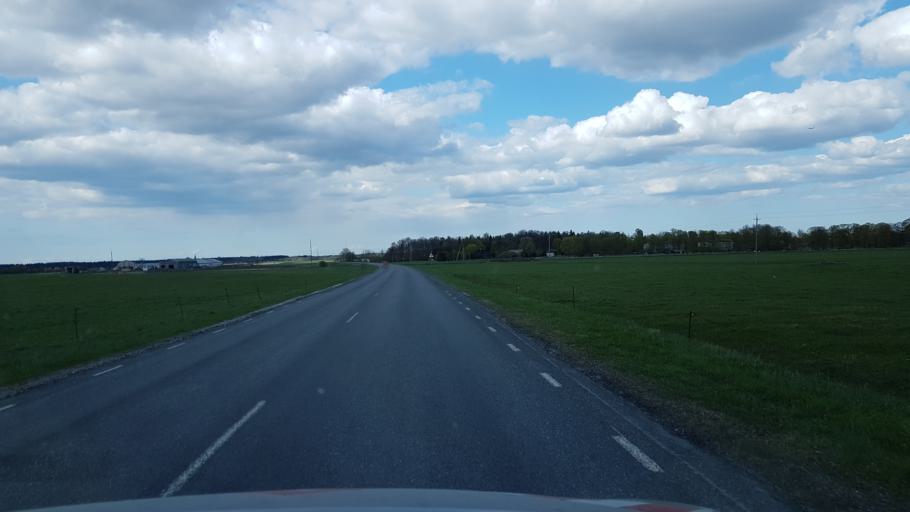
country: EE
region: Harju
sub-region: Keila linn
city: Keila
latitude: 59.2714
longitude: 24.4529
